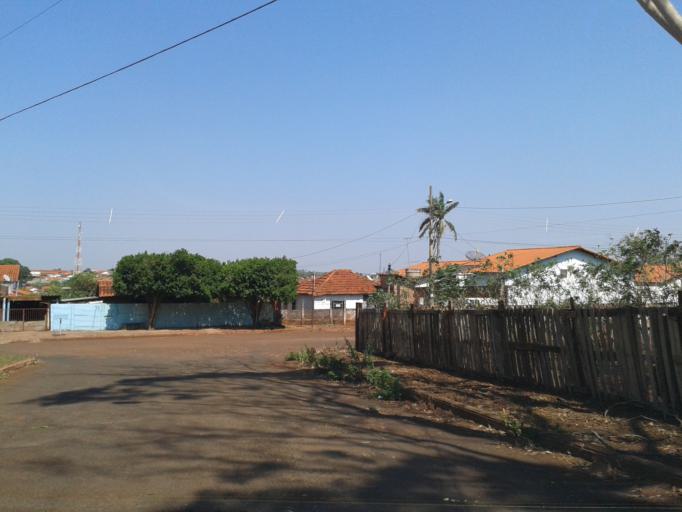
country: BR
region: Minas Gerais
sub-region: Ituiutaba
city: Ituiutaba
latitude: -18.9558
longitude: -49.4507
